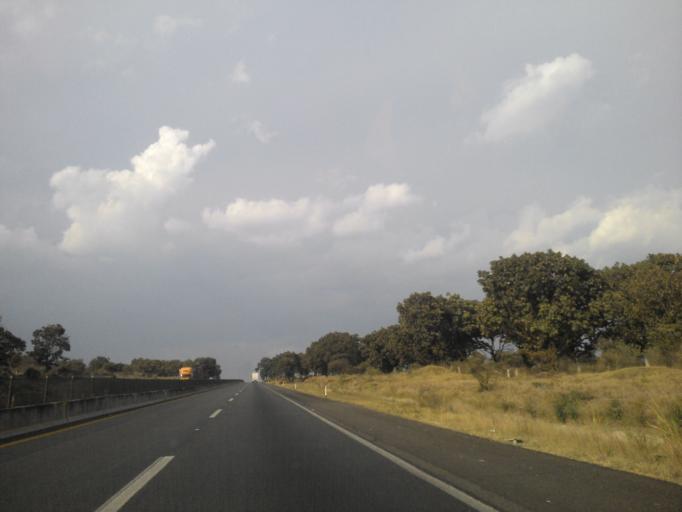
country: MX
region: Jalisco
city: Tepatitlan de Morelos
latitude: 20.8531
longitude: -102.7730
